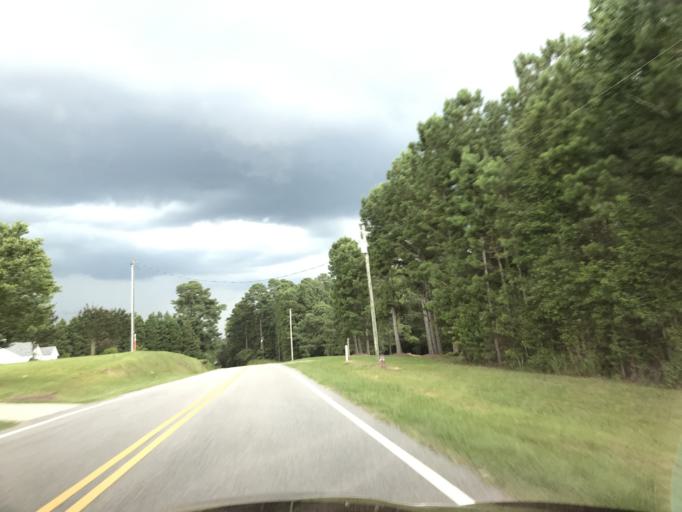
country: US
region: North Carolina
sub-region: Johnston County
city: Four Oaks
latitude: 35.5128
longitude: -78.4725
